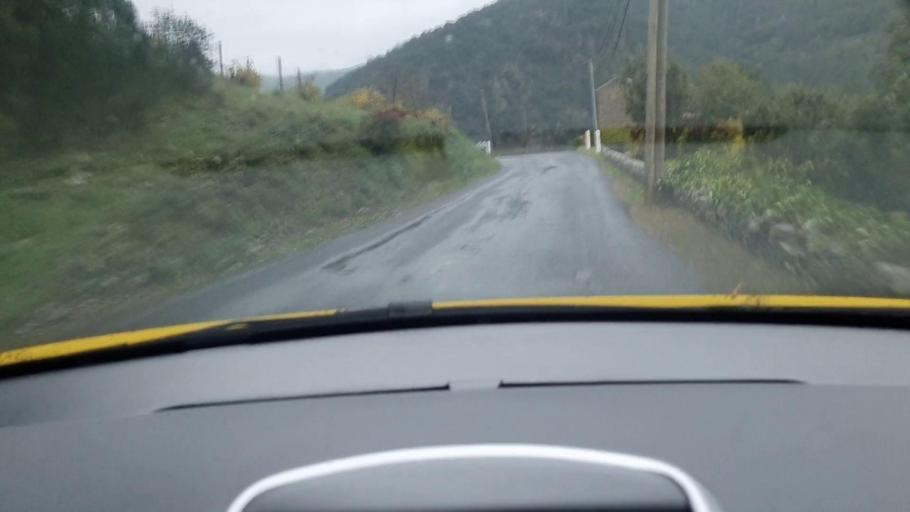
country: FR
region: Languedoc-Roussillon
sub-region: Departement du Gard
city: Sumene
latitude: 44.0166
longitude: 3.7221
